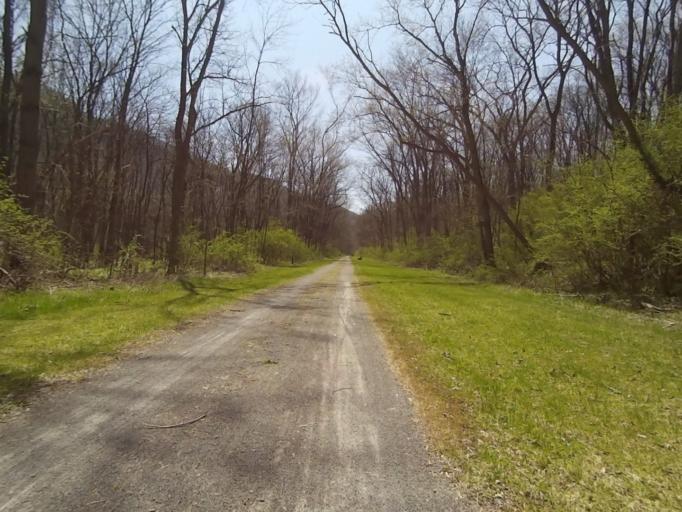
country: US
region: Pennsylvania
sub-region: Blair County
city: Williamsburg
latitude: 40.4951
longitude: -78.1669
